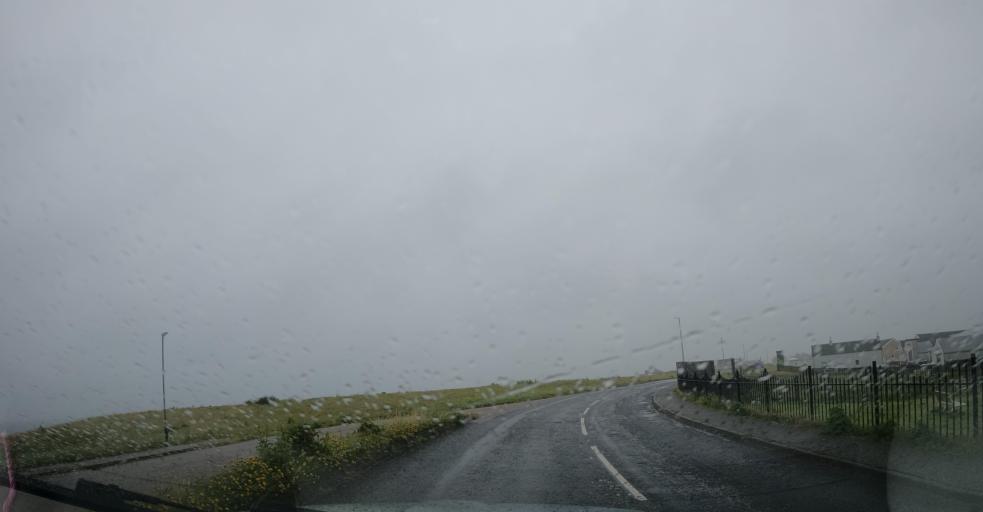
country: GB
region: Scotland
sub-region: Eilean Siar
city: Benbecula
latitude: 57.4735
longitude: -7.3919
